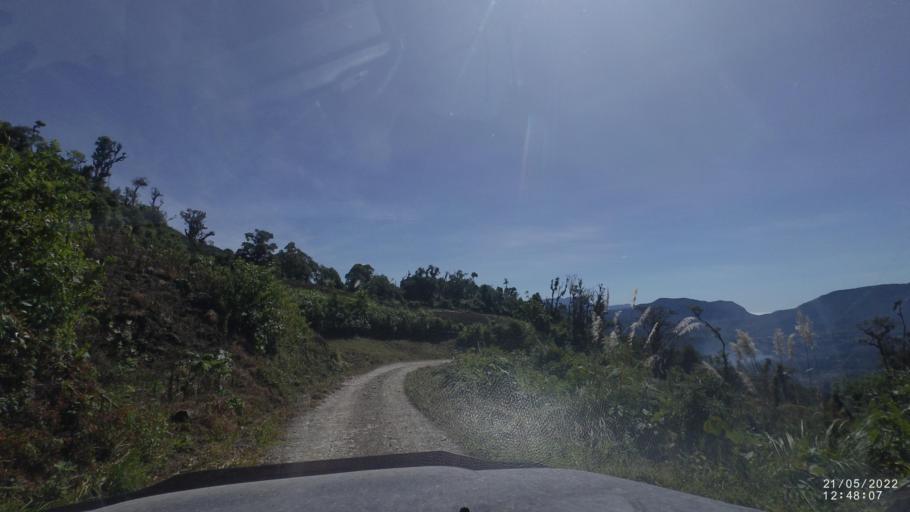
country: BO
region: Cochabamba
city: Colomi
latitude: -17.1811
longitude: -65.9425
